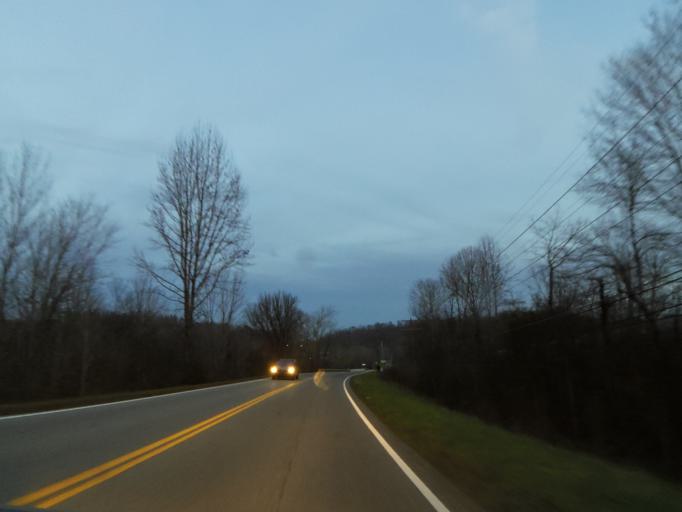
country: US
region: Tennessee
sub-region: Morgan County
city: Coalfield
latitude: 35.9703
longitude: -84.4763
